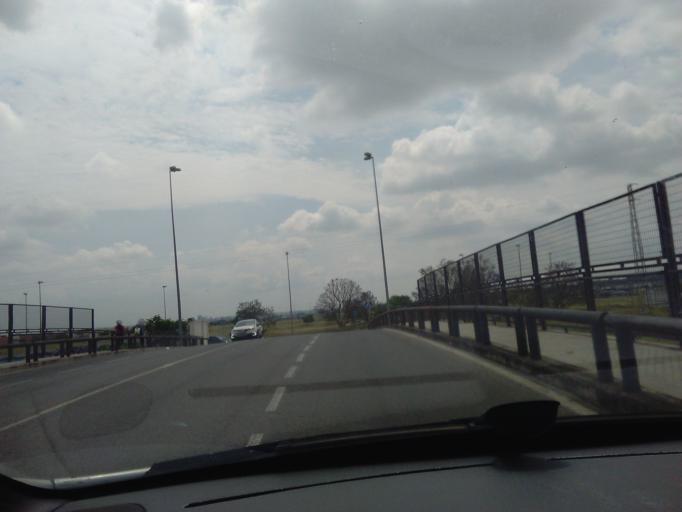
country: ES
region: Andalusia
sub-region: Provincia de Sevilla
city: Sevilla
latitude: 37.3716
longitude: -5.9390
